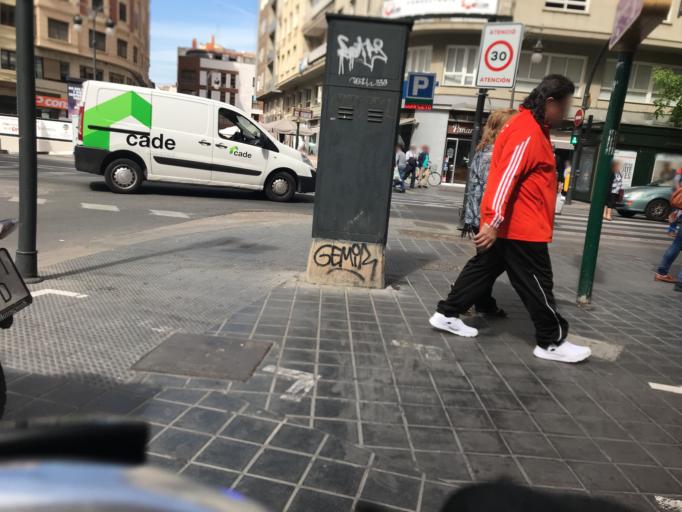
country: ES
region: Valencia
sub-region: Provincia de Valencia
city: Valencia
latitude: 39.4713
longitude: -0.3794
